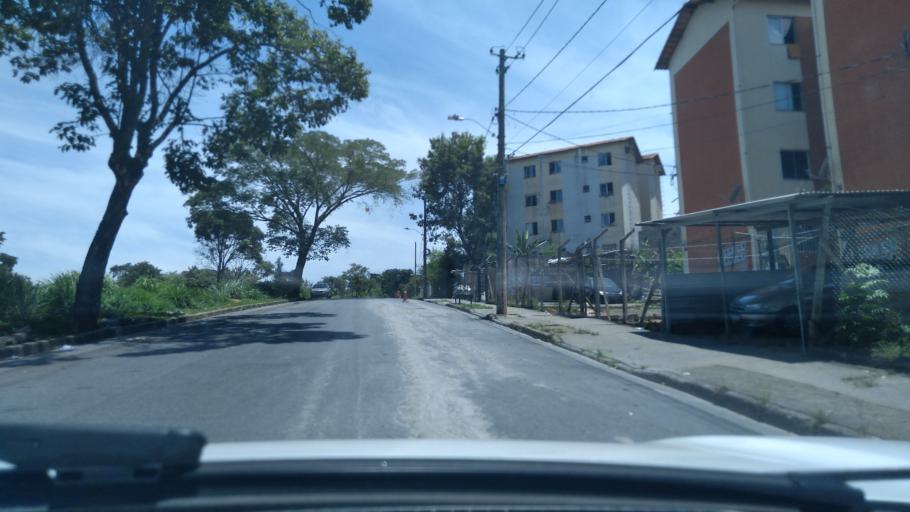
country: BR
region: Minas Gerais
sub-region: Contagem
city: Contagem
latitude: -19.9275
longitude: -44.0174
